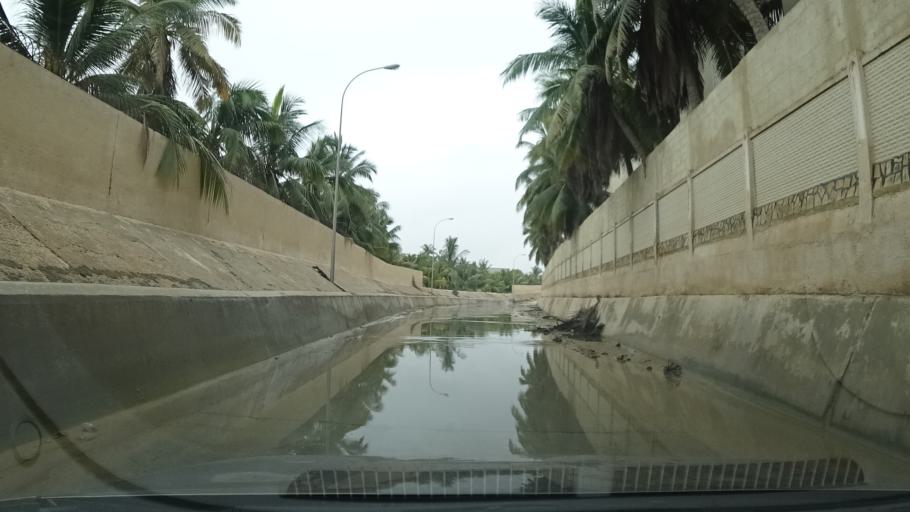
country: OM
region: Zufar
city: Salalah
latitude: 17.0081
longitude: 54.0668
